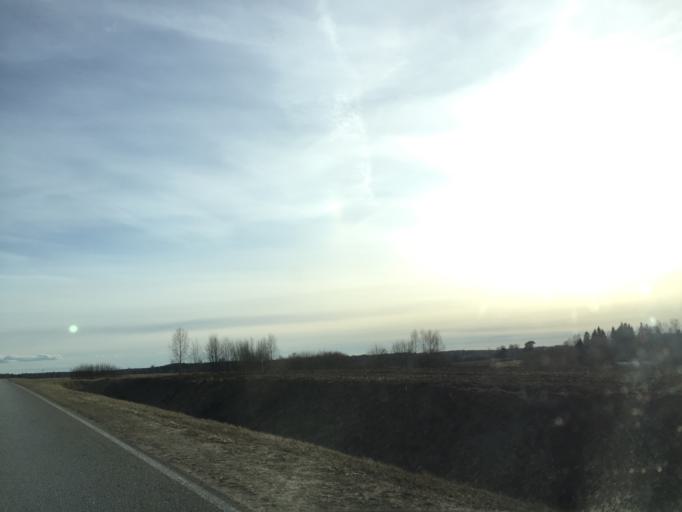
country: LV
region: Sigulda
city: Sigulda
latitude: 57.1708
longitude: 24.8140
